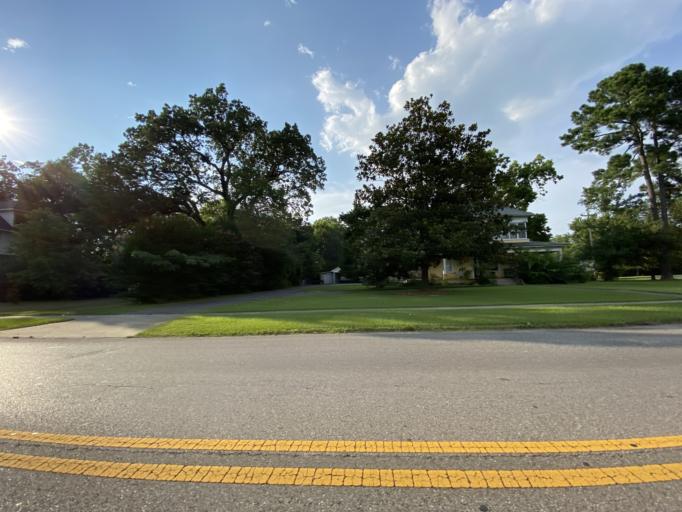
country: US
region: Alabama
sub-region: Morgan County
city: Hartselle
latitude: 34.4449
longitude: -86.9302
